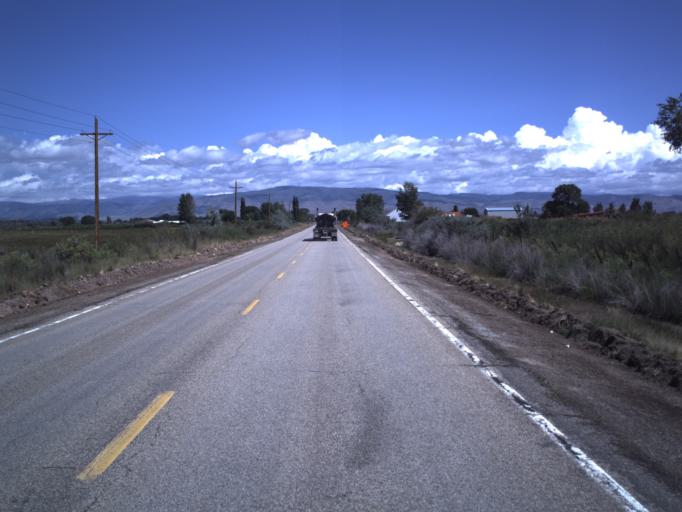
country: US
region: Utah
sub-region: Duchesne County
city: Roosevelt
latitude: 40.4143
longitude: -110.0299
